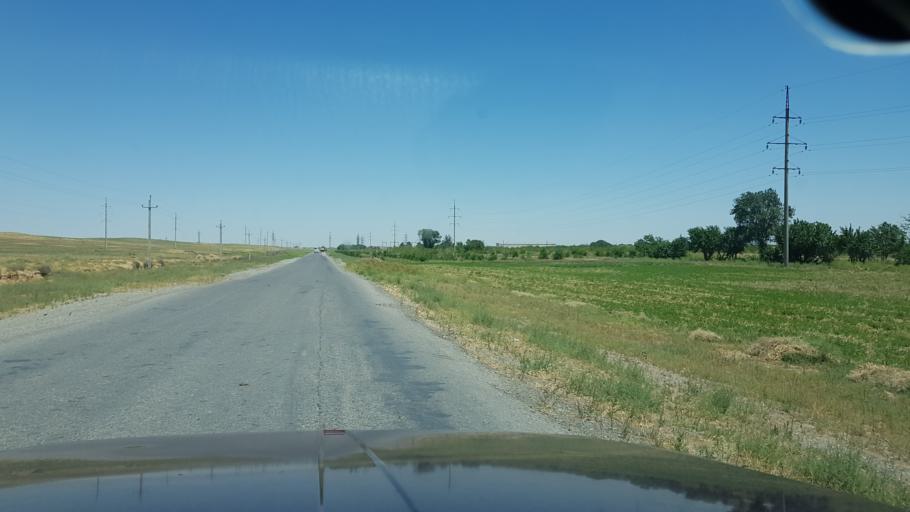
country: TM
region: Ahal
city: Annau
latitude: 37.8770
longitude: 58.7246
